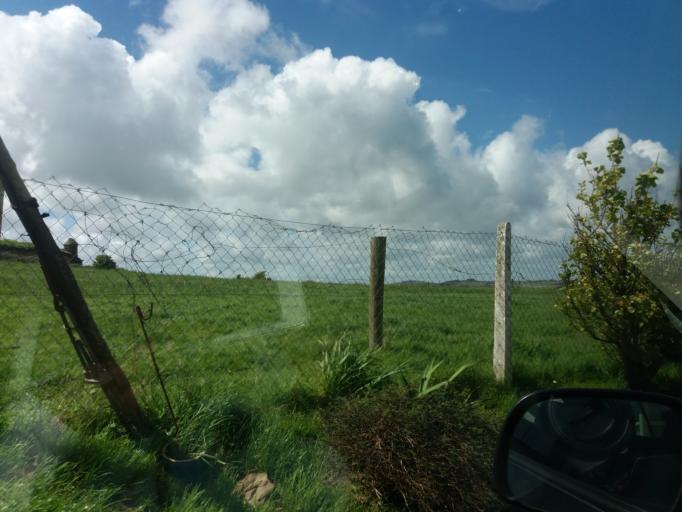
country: IE
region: Munster
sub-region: Waterford
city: Dunmore East
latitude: 52.2214
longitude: -6.9353
